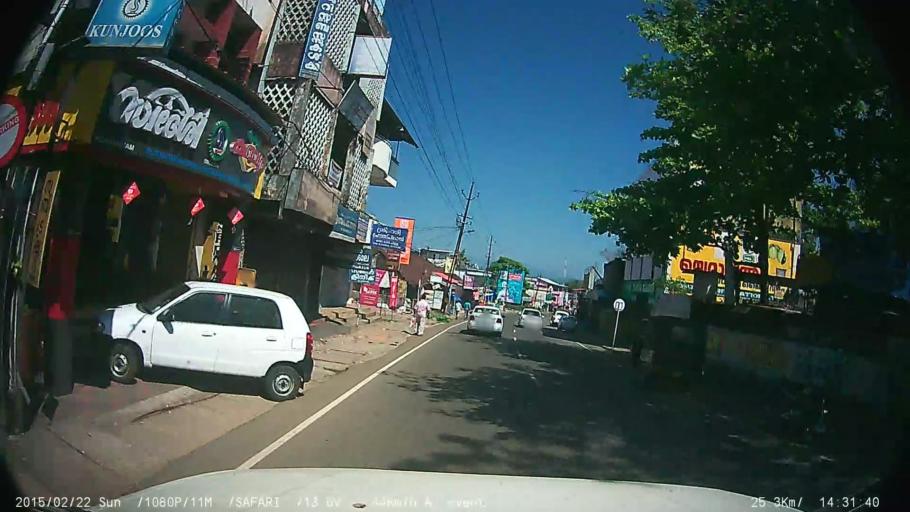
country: IN
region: Kerala
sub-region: Kottayam
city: Erattupetta
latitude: 9.5648
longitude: 76.7561
